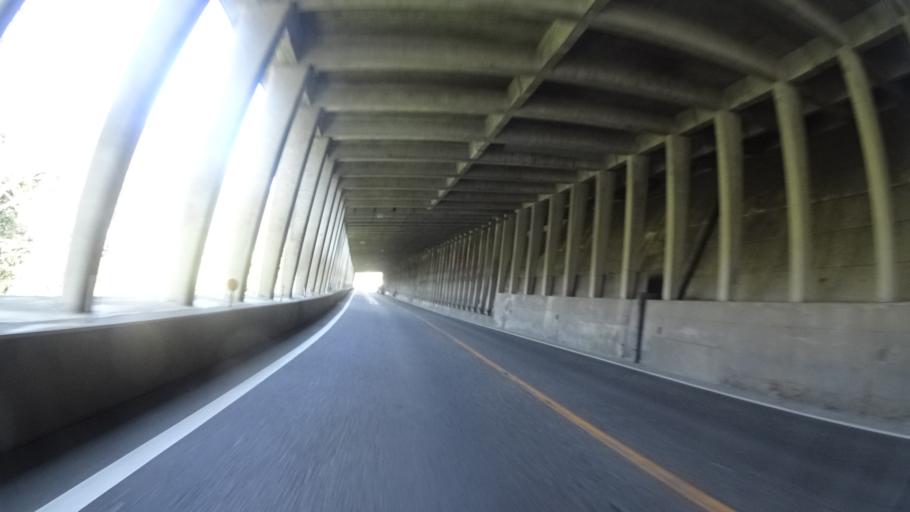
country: JP
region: Ishikawa
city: Tsurugi-asahimachi
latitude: 36.4079
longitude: 136.6331
